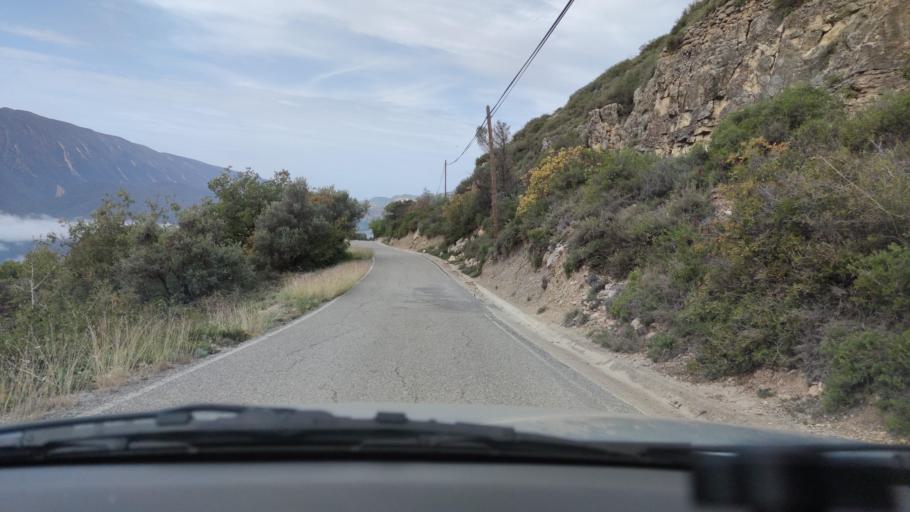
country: ES
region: Catalonia
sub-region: Provincia de Lleida
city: Llimiana
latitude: 42.0684
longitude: 0.9232
